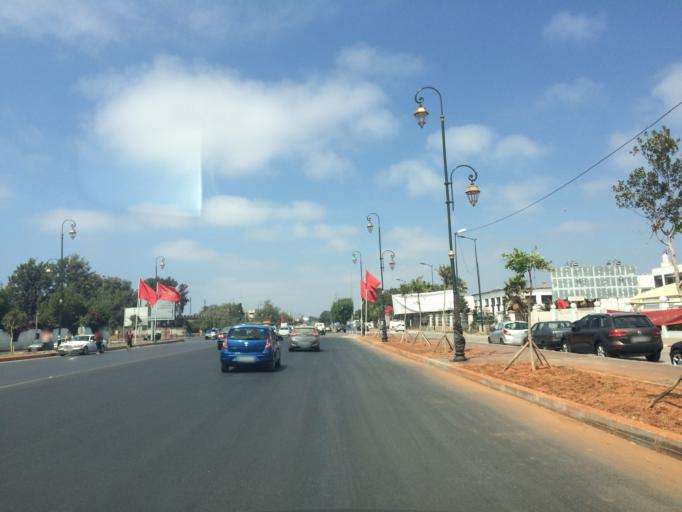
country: MA
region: Rabat-Sale-Zemmour-Zaer
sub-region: Skhirate-Temara
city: Temara
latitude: 33.9753
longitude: -6.8780
